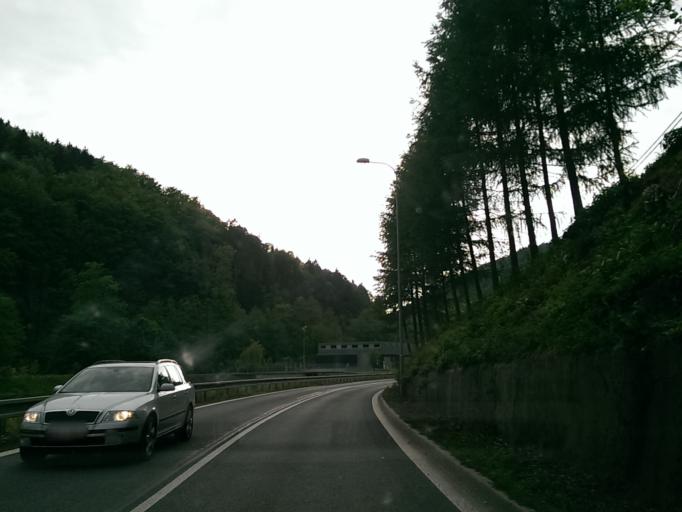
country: CZ
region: Liberecky
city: Zelezny Brod
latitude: 50.6413
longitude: 15.2399
